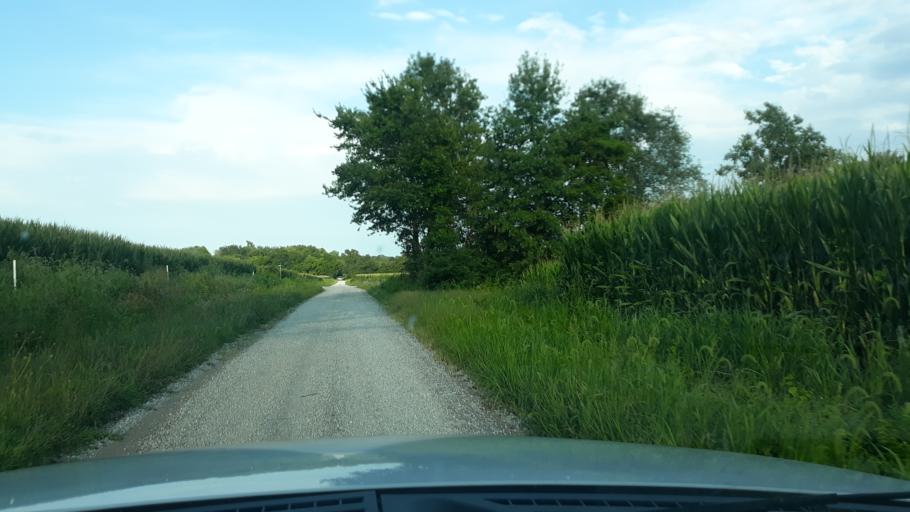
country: US
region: Illinois
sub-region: Saline County
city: Eldorado
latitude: 37.8343
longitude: -88.5124
